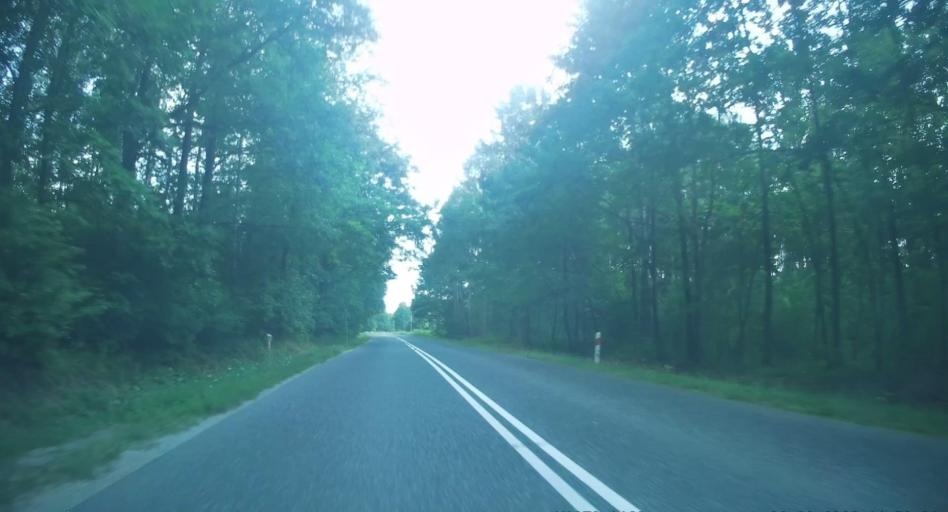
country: PL
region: Swietokrzyskie
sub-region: Powiat kielecki
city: Lopuszno
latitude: 50.8864
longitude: 20.2602
